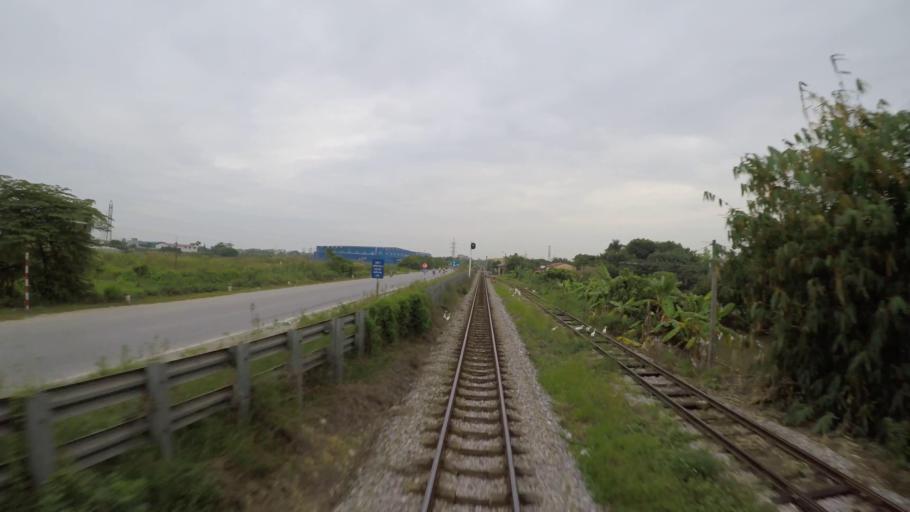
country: VN
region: Hung Yen
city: Ban Yen Nhan
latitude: 20.9854
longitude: 106.0489
